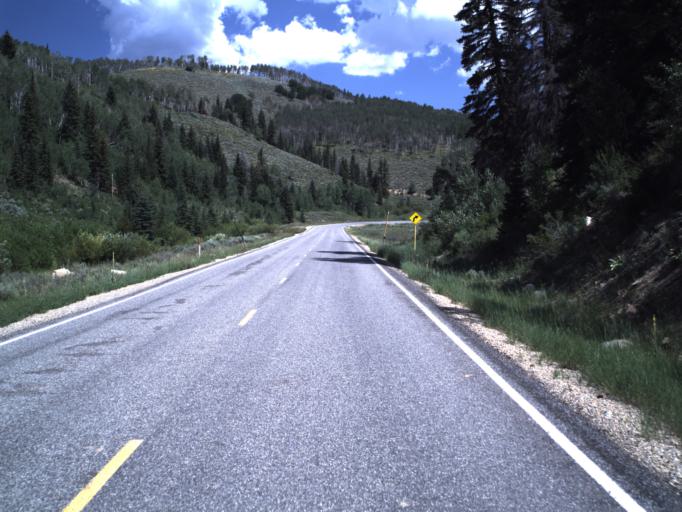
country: US
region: Utah
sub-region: Sanpete County
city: Fairview
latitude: 39.6605
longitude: -111.1554
